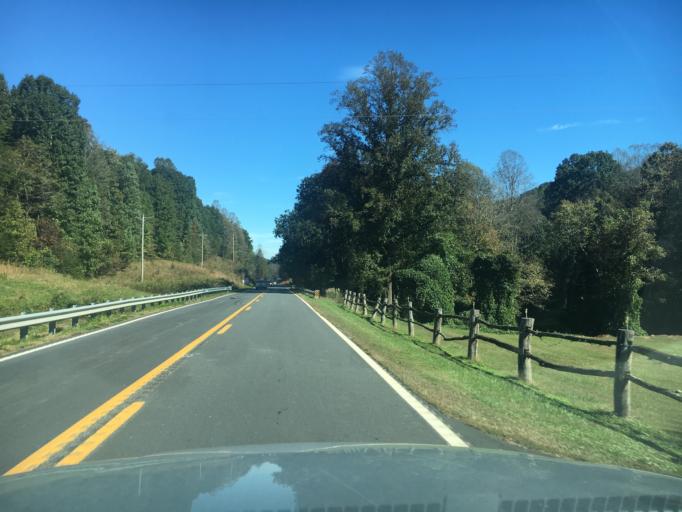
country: US
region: North Carolina
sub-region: Burke County
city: Glen Alpine
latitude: 35.6213
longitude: -81.8062
